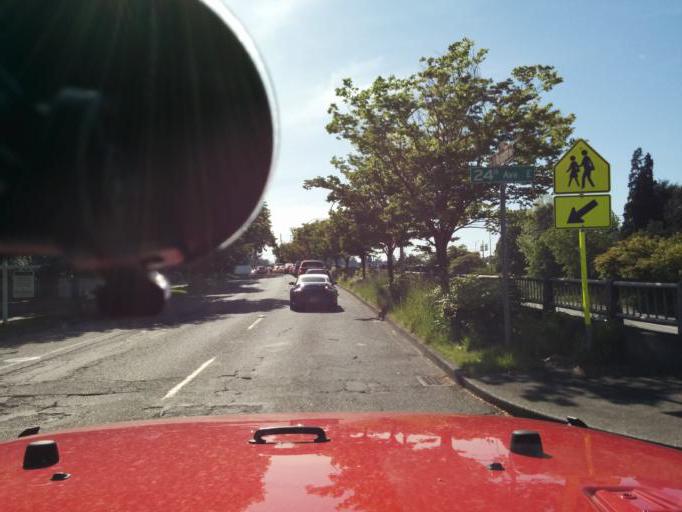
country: US
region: Washington
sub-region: King County
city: Seattle
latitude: 47.6442
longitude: -122.3021
